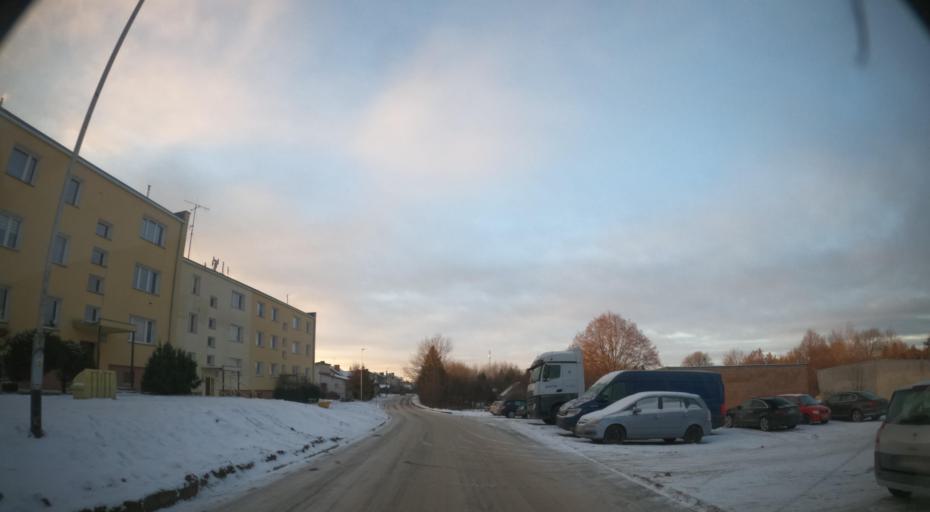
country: PL
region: West Pomeranian Voivodeship
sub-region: Powiat koszalinski
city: Sianow
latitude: 54.2341
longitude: 16.3078
